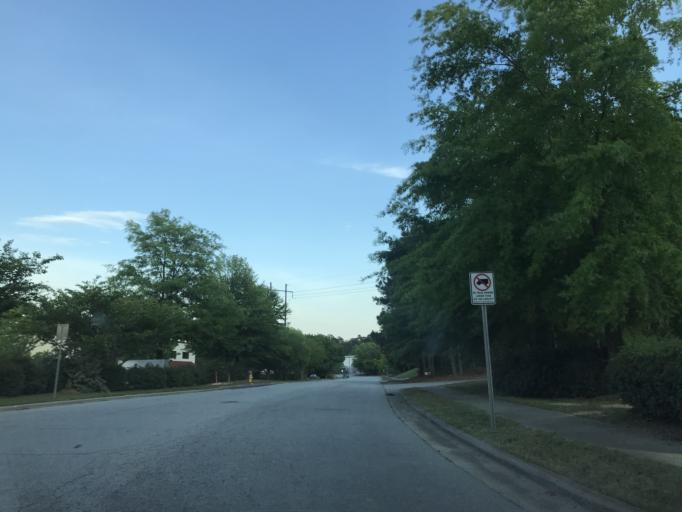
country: US
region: North Carolina
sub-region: Wake County
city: Knightdale
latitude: 35.7672
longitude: -78.5537
